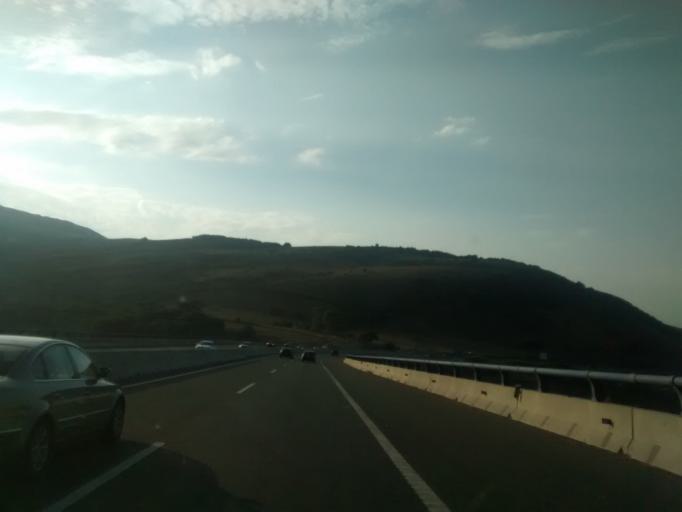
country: ES
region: Cantabria
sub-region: Provincia de Cantabria
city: Santiurde de Reinosa
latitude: 43.0570
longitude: -4.0883
